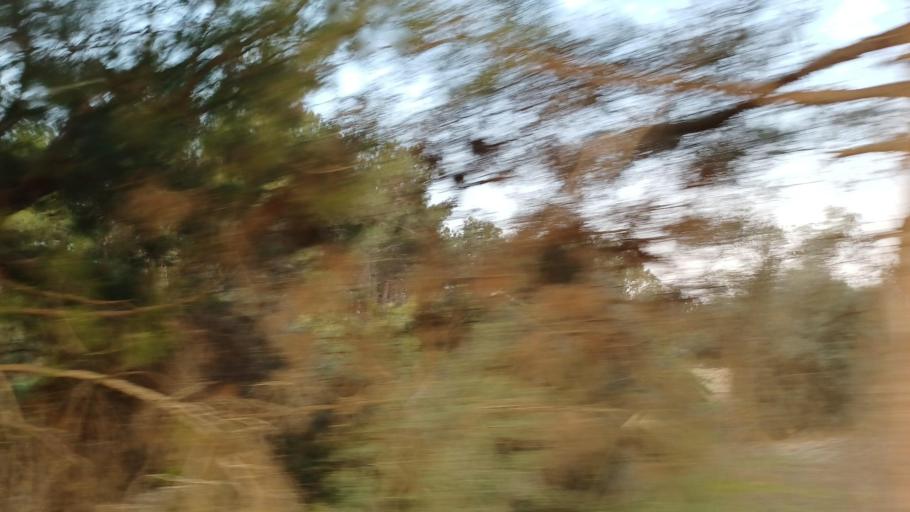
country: CY
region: Larnaka
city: Mosfiloti
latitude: 34.9433
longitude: 33.4142
